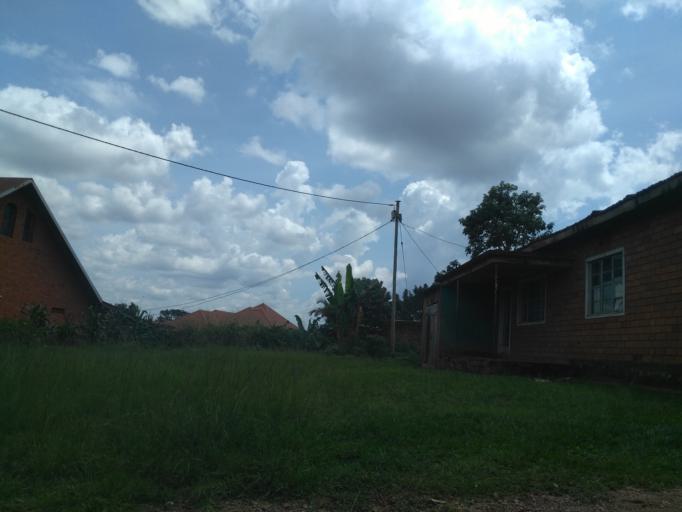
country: UG
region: Central Region
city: Kampala Central Division
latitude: 0.3585
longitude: 32.5834
